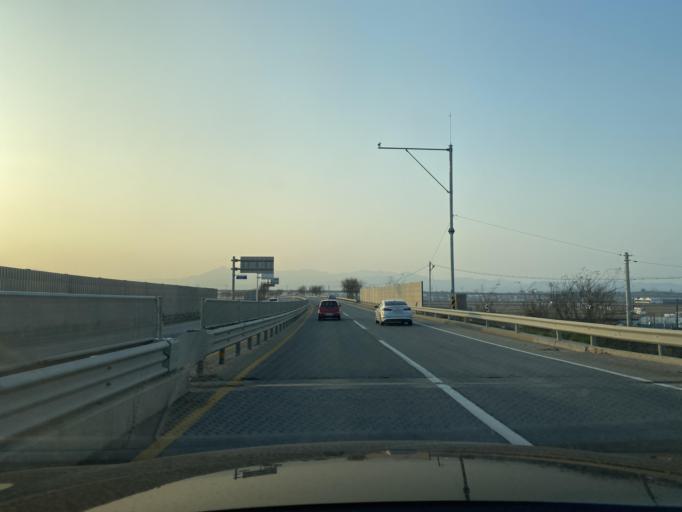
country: KR
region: Chungcheongnam-do
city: Yesan
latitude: 36.6920
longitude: 126.7344
